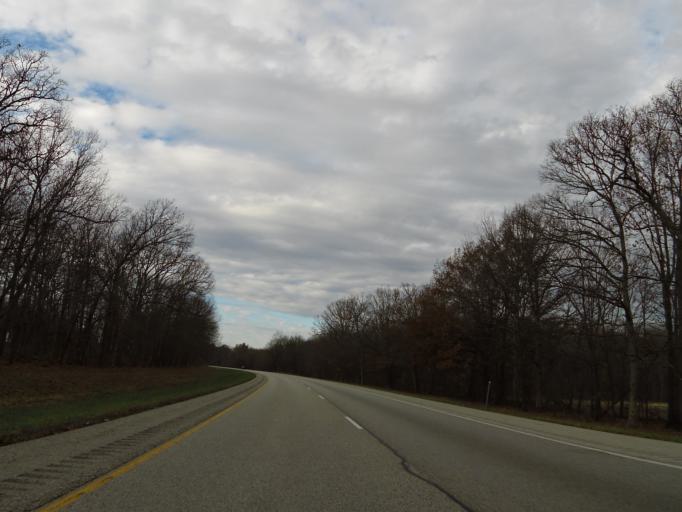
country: US
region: Illinois
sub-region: Washington County
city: Nashville
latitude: 38.3925
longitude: -89.3143
